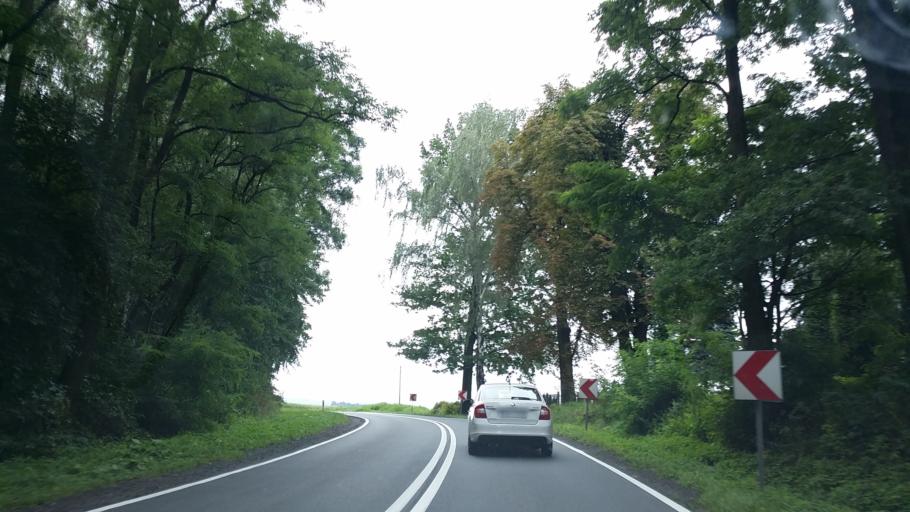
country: PL
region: Lesser Poland Voivodeship
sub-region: Powiat oswiecimski
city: Zator
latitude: 49.9578
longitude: 19.4427
